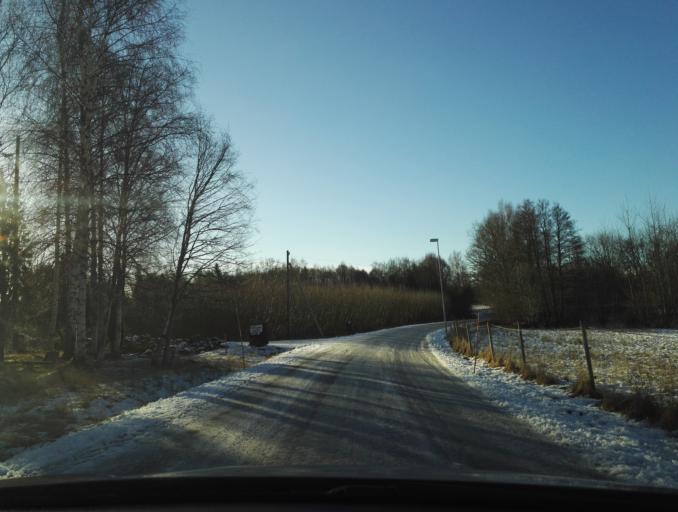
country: SE
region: Kronoberg
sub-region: Vaxjo Kommun
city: Gemla
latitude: 56.8307
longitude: 14.5886
